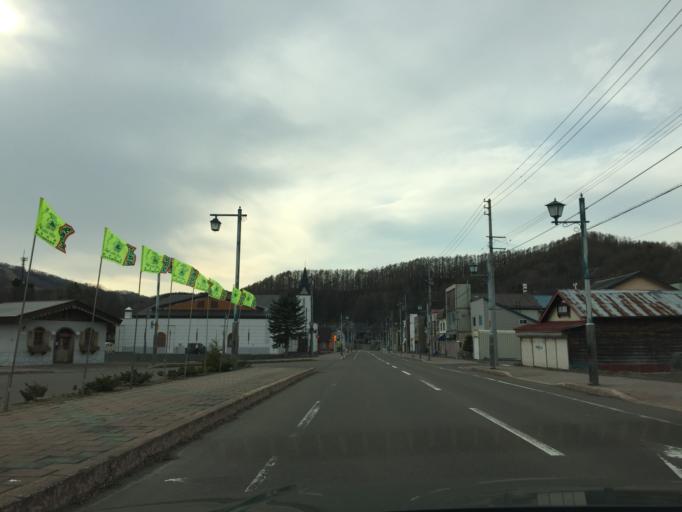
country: JP
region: Hokkaido
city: Utashinai
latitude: 43.5211
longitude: 142.0430
